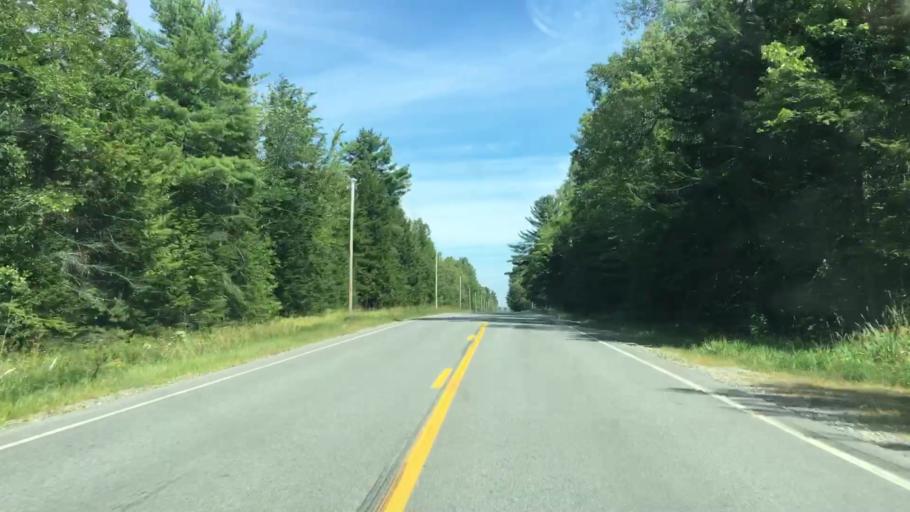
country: US
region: Maine
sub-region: Penobscot County
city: Howland
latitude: 45.2321
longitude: -68.6969
